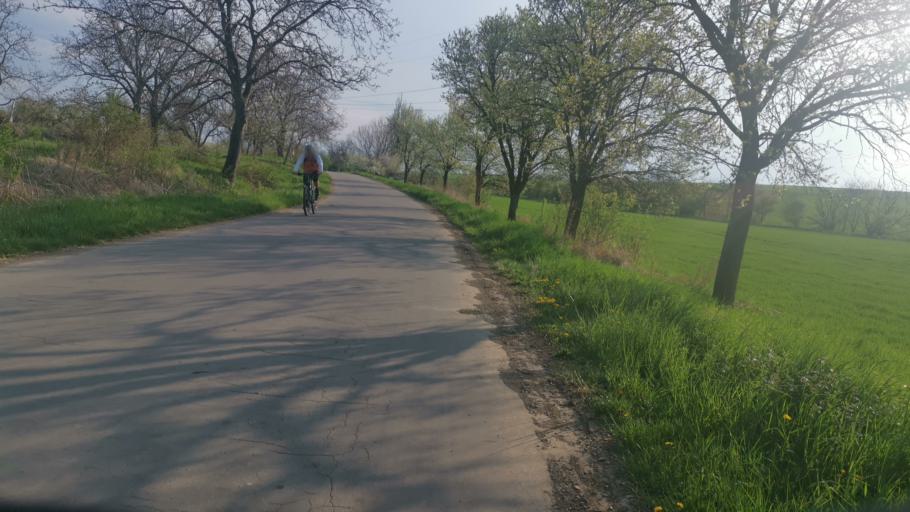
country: CZ
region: South Moravian
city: Petrov
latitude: 48.8581
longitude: 17.3085
